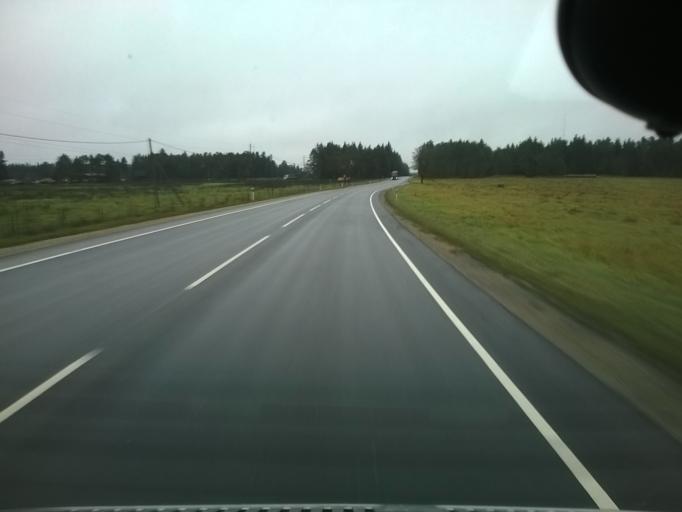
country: EE
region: Harju
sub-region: Nissi vald
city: Turba
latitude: 59.0273
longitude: 24.1511
